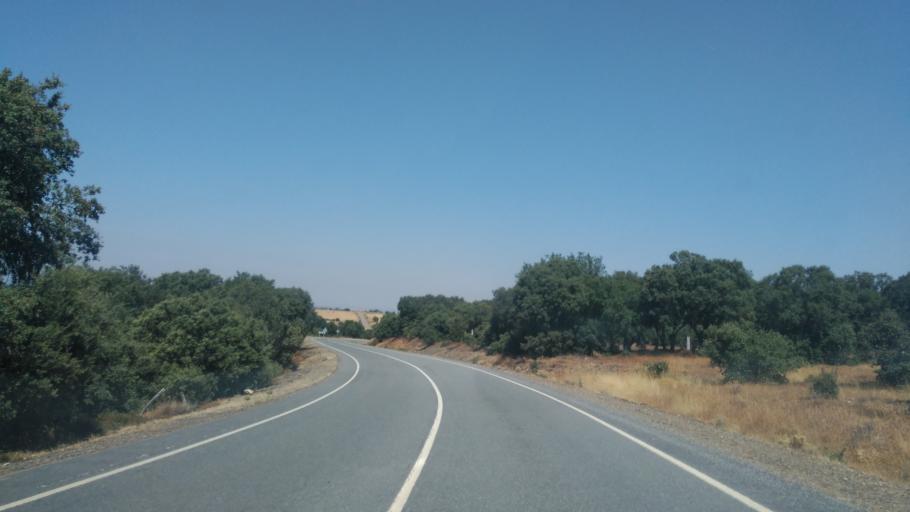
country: ES
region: Castille and Leon
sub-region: Provincia de Salamanca
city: Aldeanueva de la Sierra
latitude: 40.6099
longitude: -6.0967
